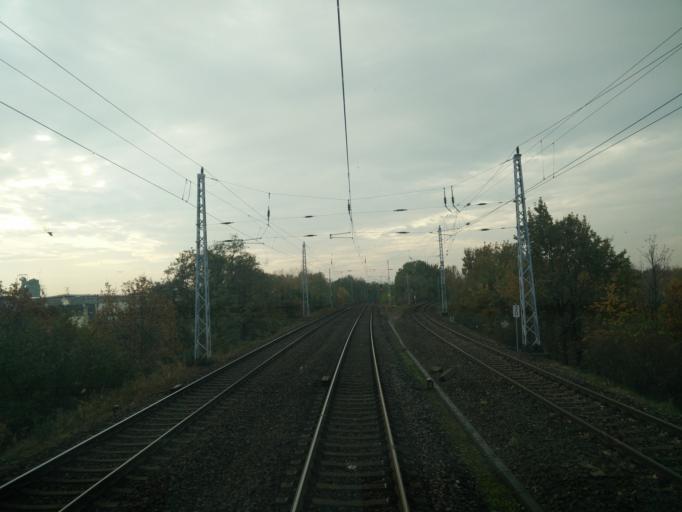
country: DE
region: Berlin
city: Adlershof
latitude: 52.4315
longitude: 13.5633
